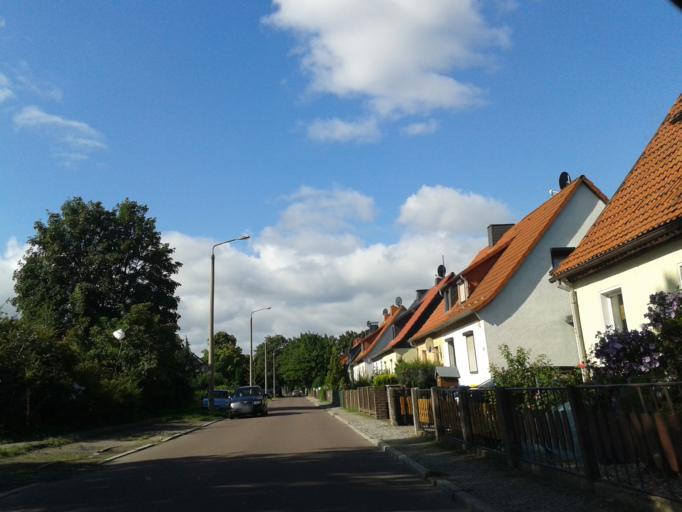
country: DE
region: Saxony-Anhalt
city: Halle (Saale)
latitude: 51.5063
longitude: 11.9977
